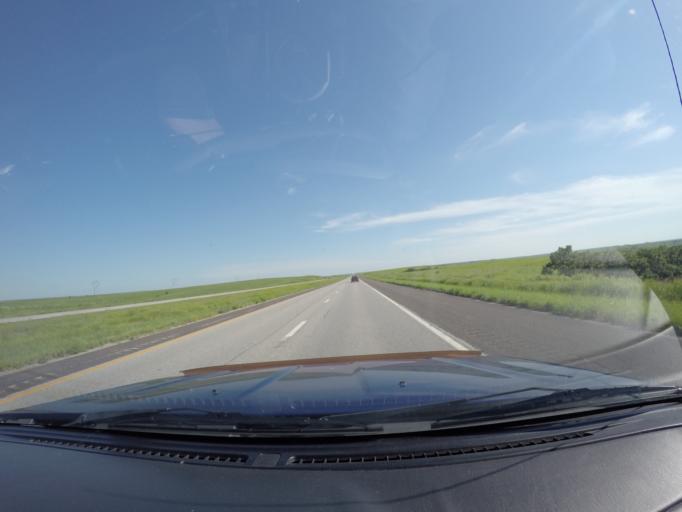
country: US
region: Kansas
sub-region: Riley County
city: Manhattan
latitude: 39.1288
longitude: -96.5384
